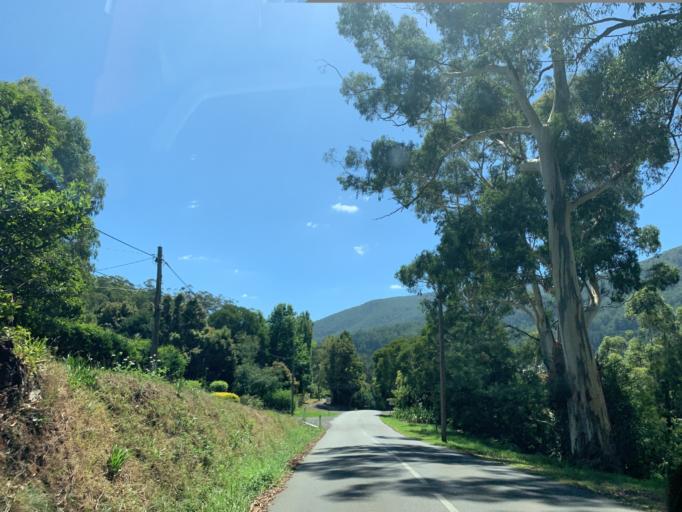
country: AU
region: Victoria
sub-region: Yarra Ranges
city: Millgrove
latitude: -37.7562
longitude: 145.6982
